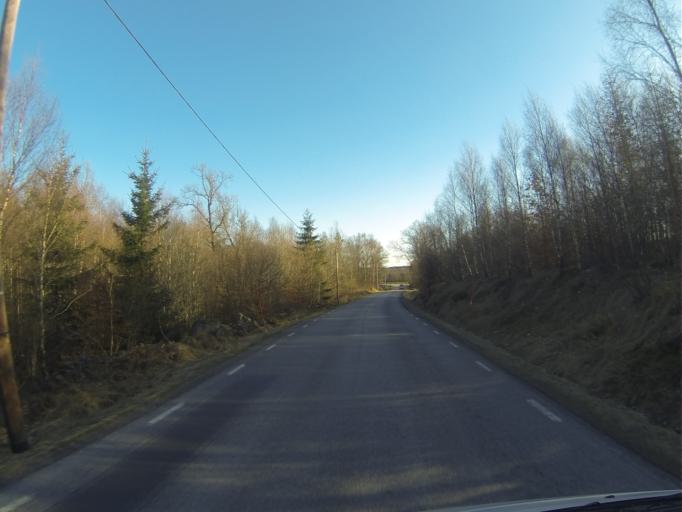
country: SE
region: Skane
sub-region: Horby Kommun
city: Hoerby
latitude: 55.8988
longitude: 13.6617
